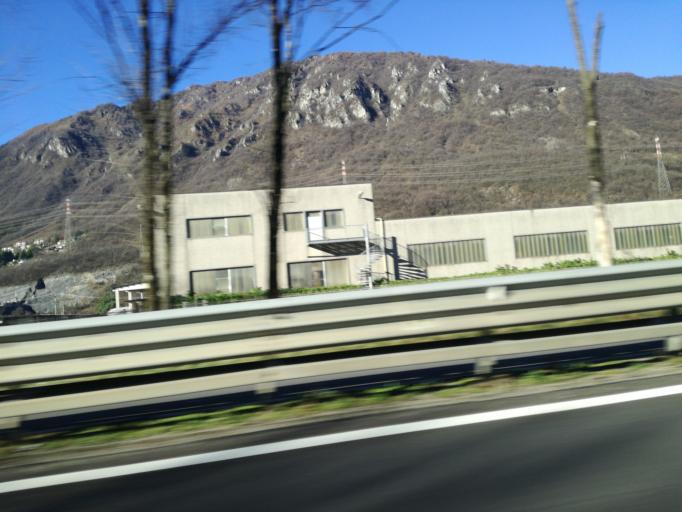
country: IT
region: Lombardy
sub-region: Provincia di Bergamo
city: Sovere
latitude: 45.8029
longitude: 10.0212
